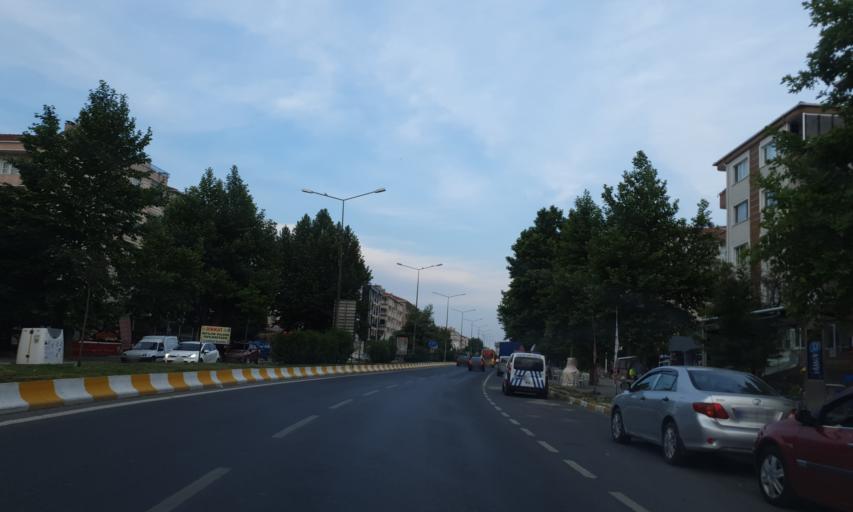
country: TR
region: Kirklareli
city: Luleburgaz
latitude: 41.4024
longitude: 27.3672
